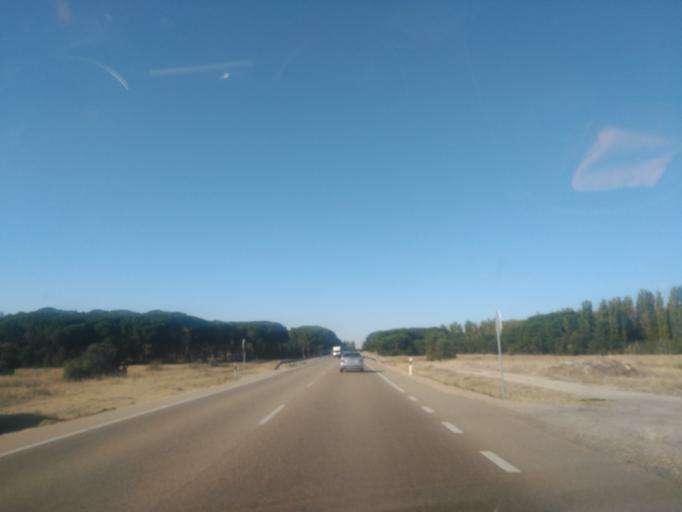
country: ES
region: Castille and Leon
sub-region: Provincia de Valladolid
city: Sardon de Duero
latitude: 41.6047
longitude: -4.4536
